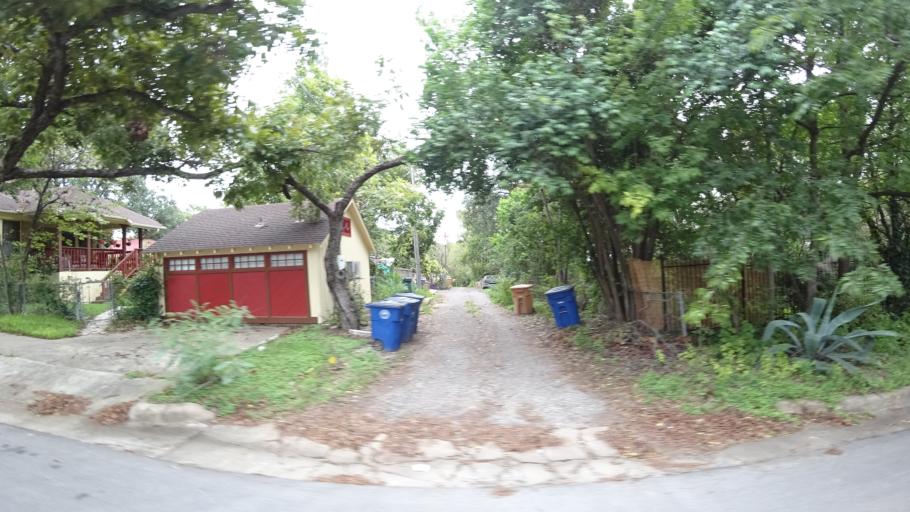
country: US
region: Texas
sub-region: Travis County
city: Austin
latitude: 30.2965
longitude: -97.7290
